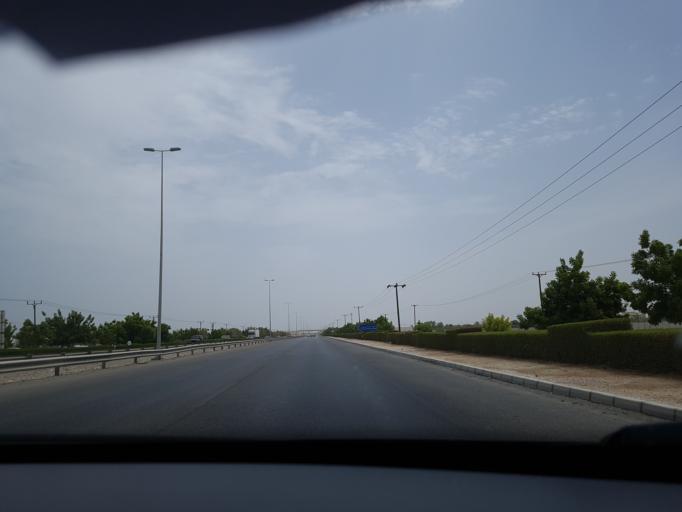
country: OM
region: Al Batinah
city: Barka'
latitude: 23.6699
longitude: 57.9728
